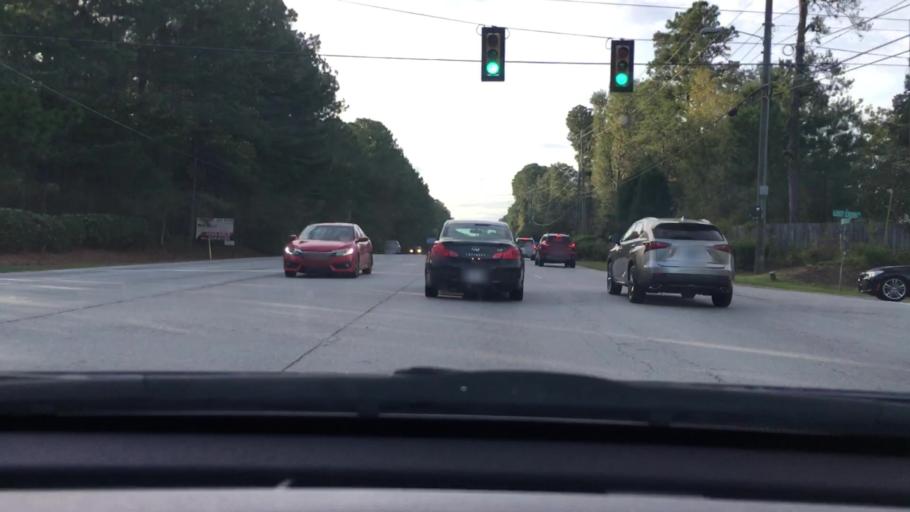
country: US
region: South Carolina
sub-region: Lexington County
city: Seven Oaks
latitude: 34.0837
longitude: -81.1382
